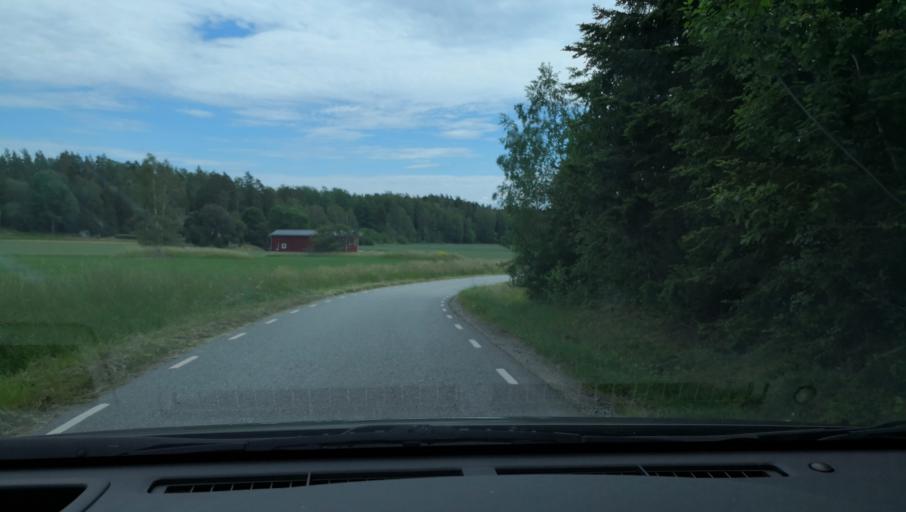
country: SE
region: Uppsala
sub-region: Enkopings Kommun
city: Orsundsbro
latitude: 59.6992
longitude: 17.4318
